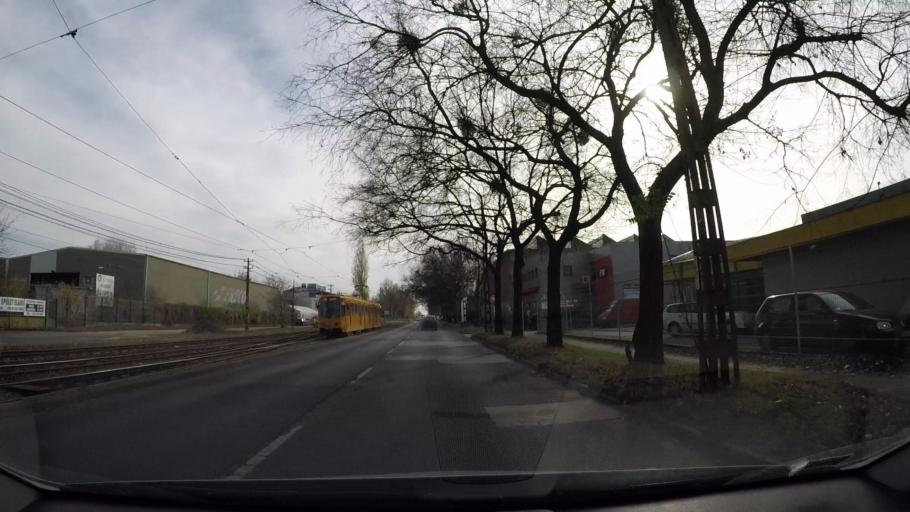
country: HU
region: Budapest
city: Budapest X. keruelet
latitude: 47.4821
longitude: 19.1594
